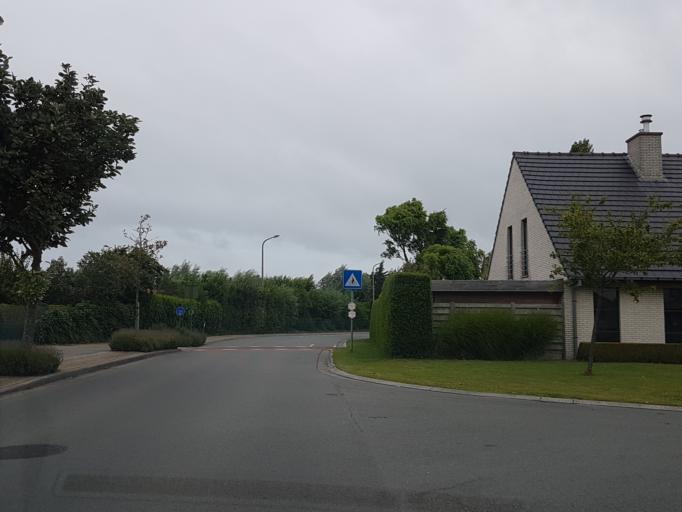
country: BE
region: Flanders
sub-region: Provincie West-Vlaanderen
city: Bredene
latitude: 51.2487
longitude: 2.9841
